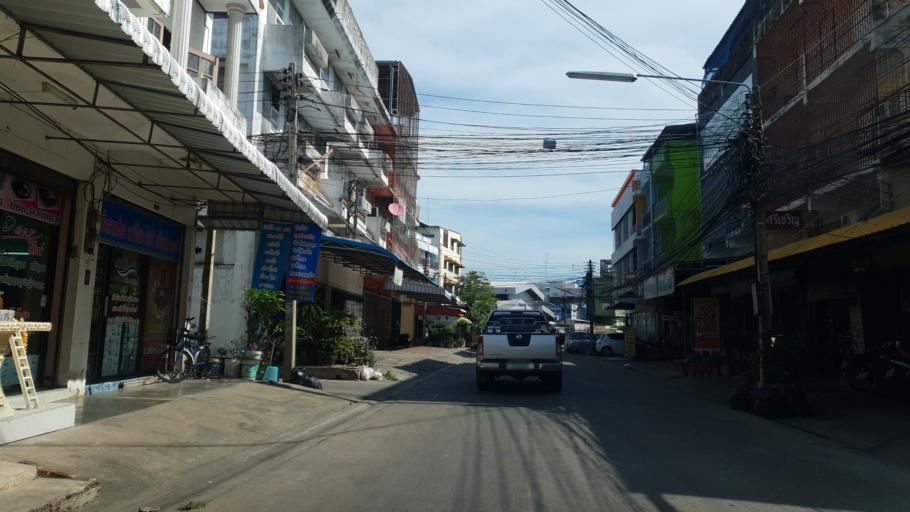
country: TH
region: Phitsanulok
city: Phitsanulok
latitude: 16.8146
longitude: 100.2704
